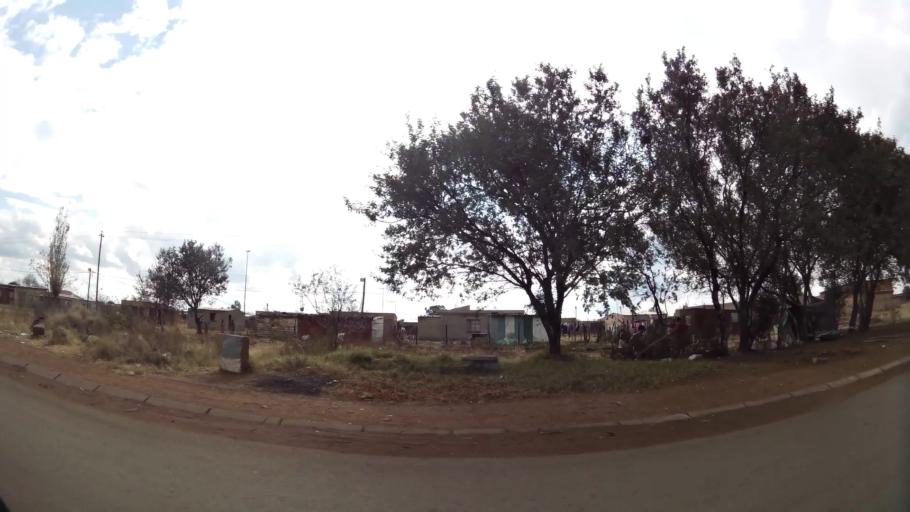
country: ZA
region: Gauteng
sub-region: Sedibeng District Municipality
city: Vanderbijlpark
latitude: -26.7012
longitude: 27.7917
